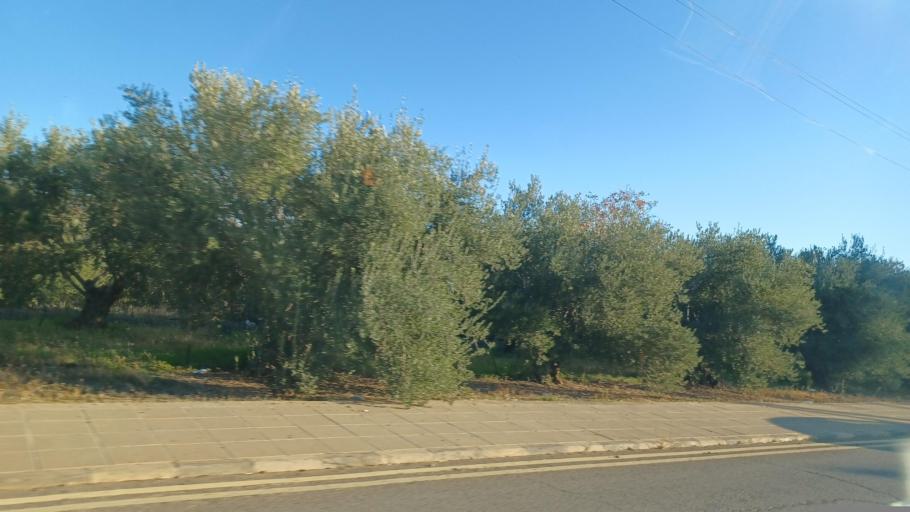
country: CY
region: Lefkosia
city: Astromeritis
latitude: 35.1403
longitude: 33.0445
